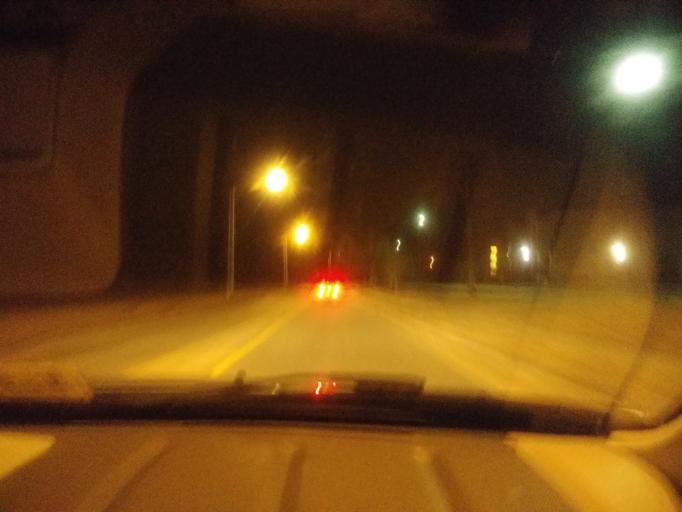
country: US
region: Virginia
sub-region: City of Chesapeake
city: Chesapeake
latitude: 36.7974
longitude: -76.1917
